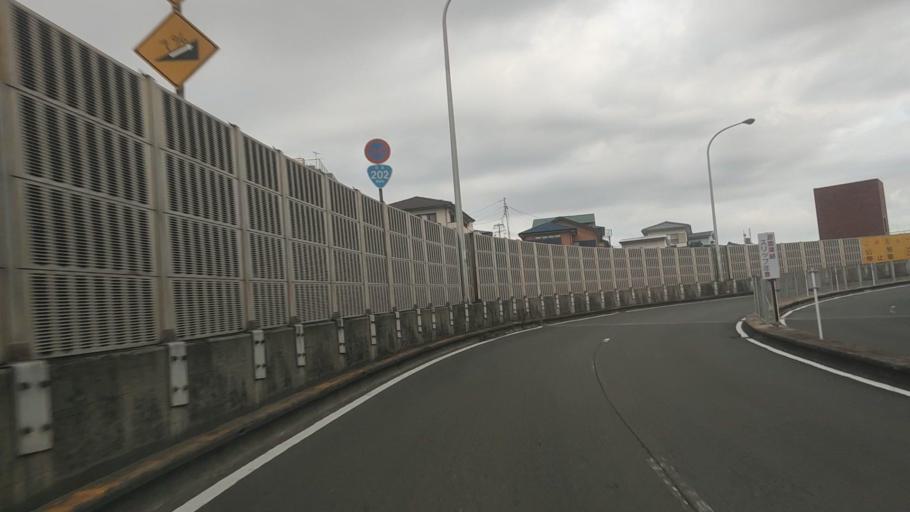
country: JP
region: Nagasaki
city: Nagasaki-shi
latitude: 32.7509
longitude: 129.8641
